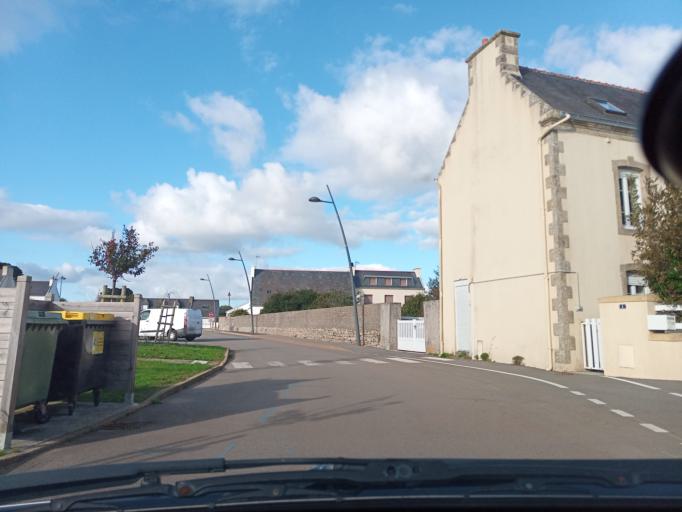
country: FR
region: Brittany
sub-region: Departement du Finistere
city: Plouhinec
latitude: 48.0137
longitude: -4.4885
